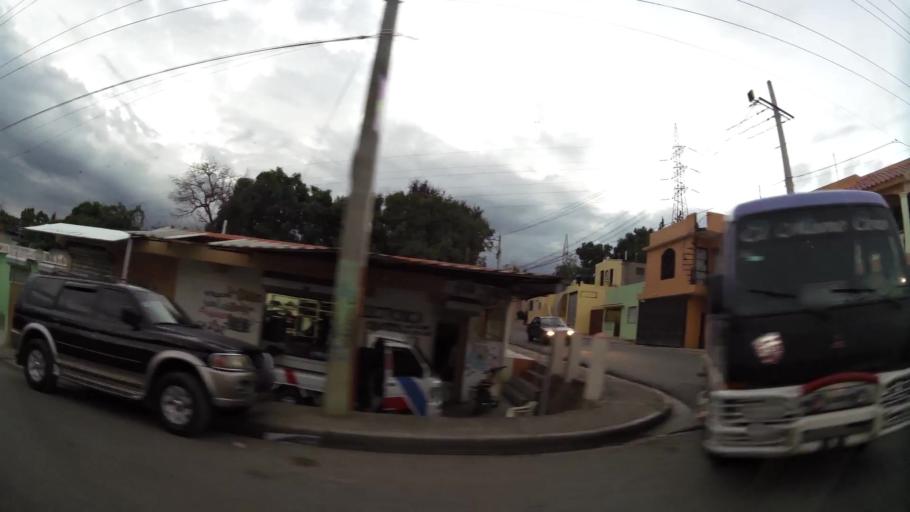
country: DO
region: Santo Domingo
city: Santo Domingo Oeste
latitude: 18.5225
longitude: -70.0339
